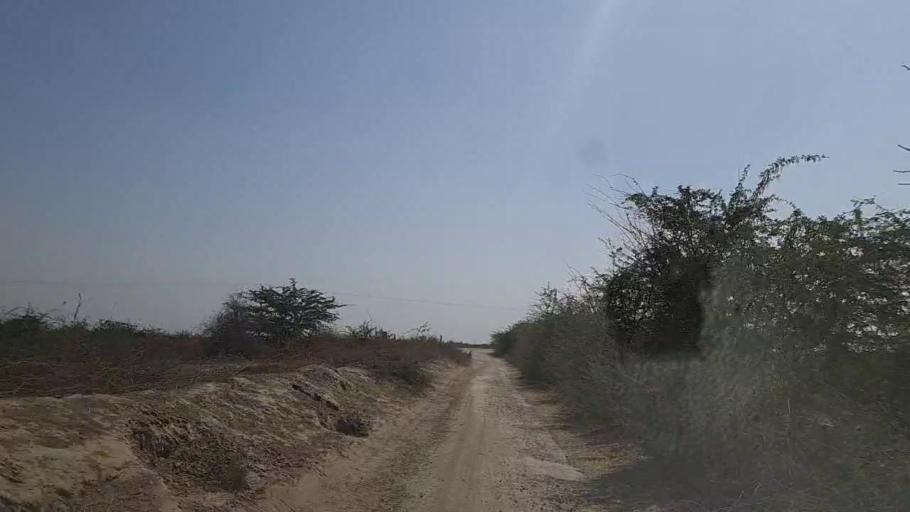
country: PK
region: Sindh
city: Naukot
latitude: 24.6251
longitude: 69.2703
